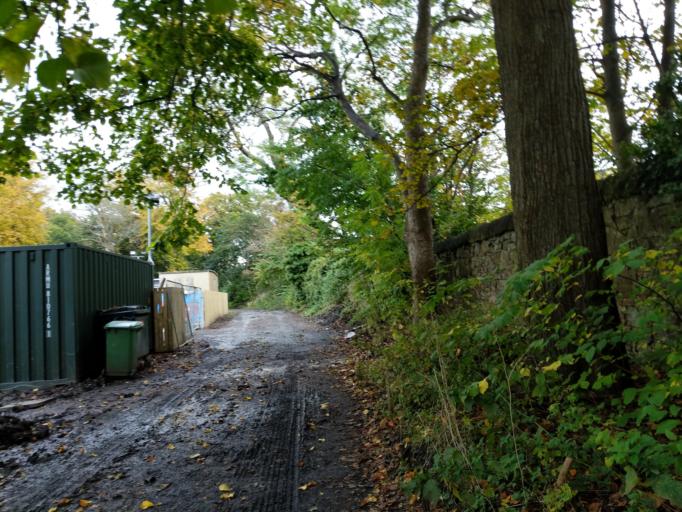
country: GB
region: Scotland
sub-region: Edinburgh
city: Edinburgh
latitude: 55.9255
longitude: -3.2186
